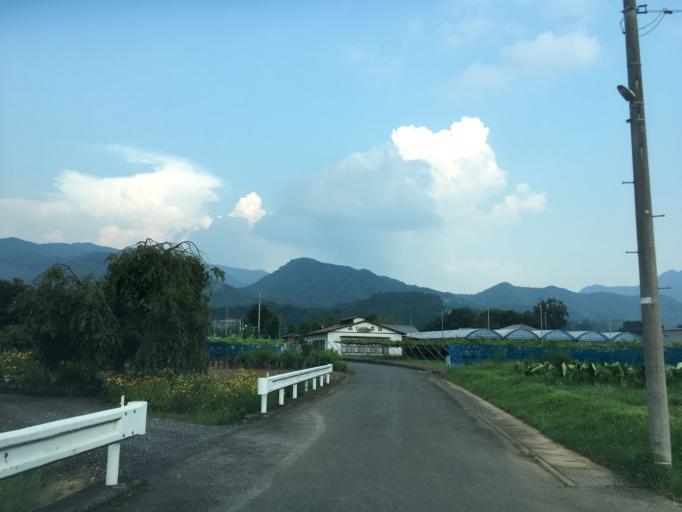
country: JP
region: Saitama
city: Chichibu
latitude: 35.9957
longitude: 139.0988
